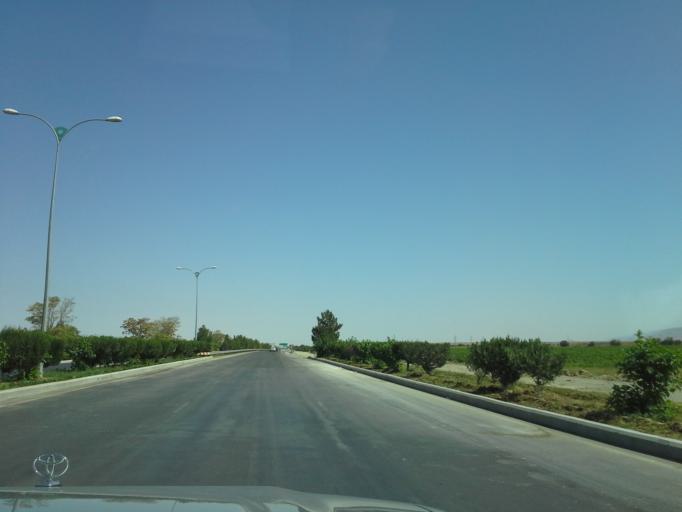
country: TM
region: Ahal
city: Annau
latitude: 37.9061
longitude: 58.5286
